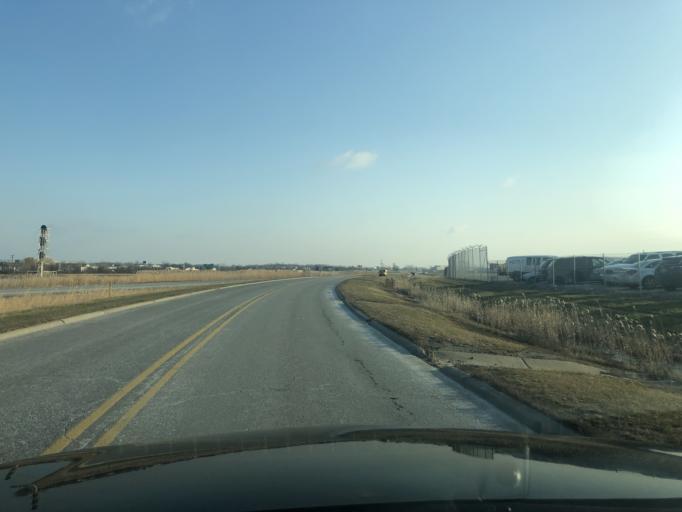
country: US
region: Michigan
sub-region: Wayne County
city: Romulus
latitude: 42.2330
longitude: -83.3543
